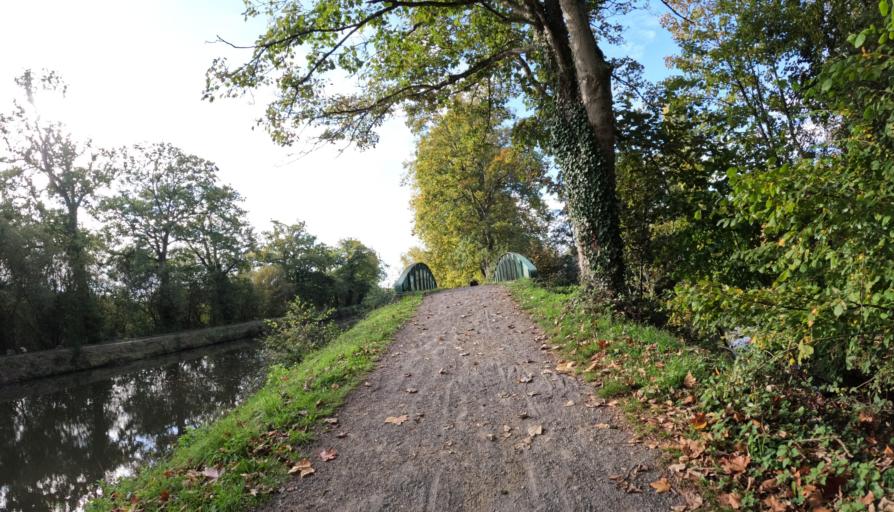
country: FR
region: Brittany
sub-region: Departement d'Ille-et-Vilaine
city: Betton
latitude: 48.1842
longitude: -1.6387
